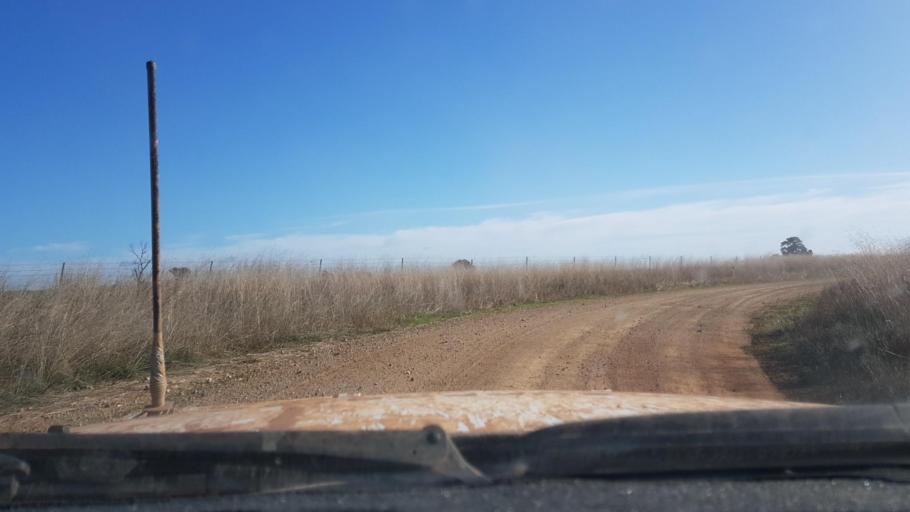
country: AU
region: New South Wales
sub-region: Junee
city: Junee
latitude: -34.9521
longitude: 147.7935
